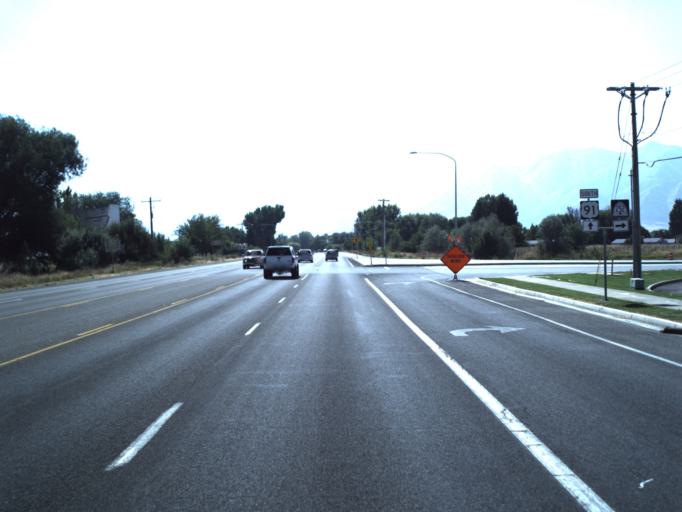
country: US
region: Utah
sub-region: Cache County
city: Nibley
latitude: 41.6980
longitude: -111.8591
